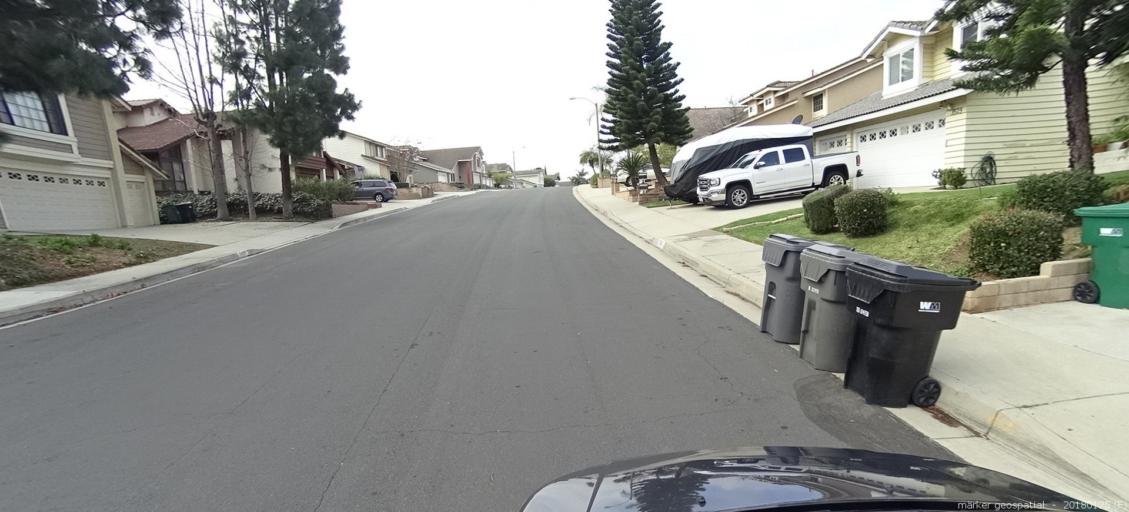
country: US
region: California
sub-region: Los Angeles County
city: Walnut
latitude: 33.9632
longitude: -117.8395
